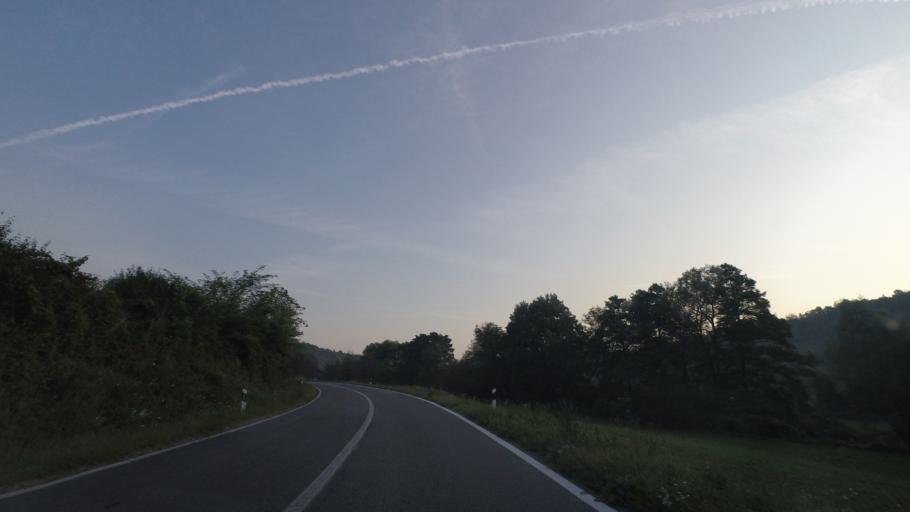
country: HR
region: Brodsko-Posavska
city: Resetari
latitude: 45.3331
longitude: 17.4567
